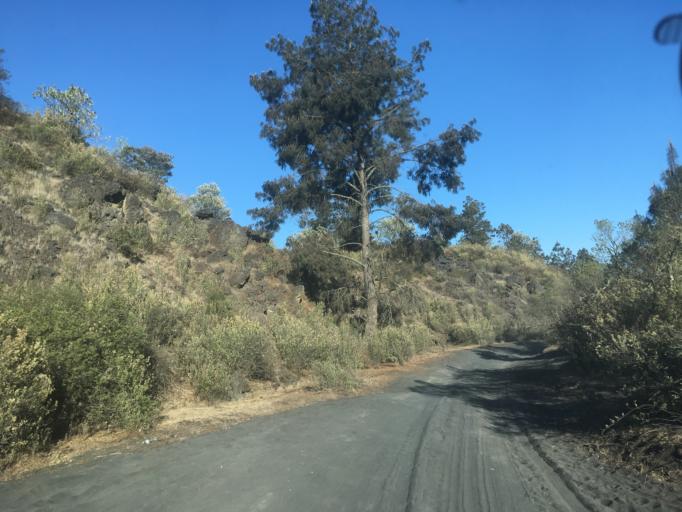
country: MX
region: Michoacan
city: Angahuan
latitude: 19.4816
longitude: -102.2506
